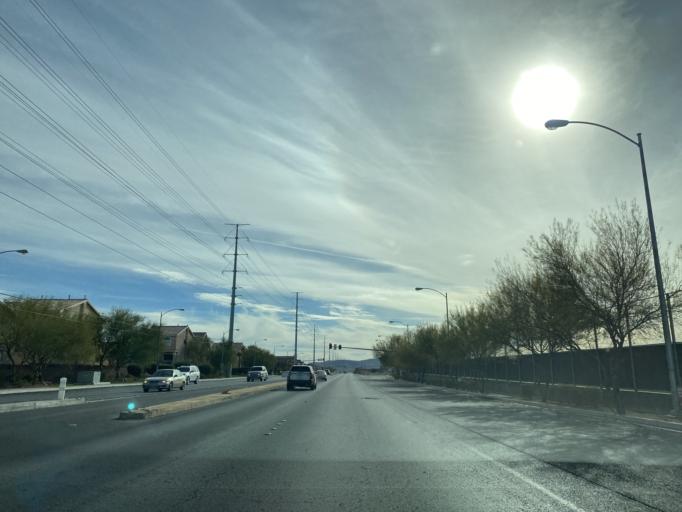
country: US
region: Nevada
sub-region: Clark County
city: Enterprise
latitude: 36.0395
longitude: -115.2436
